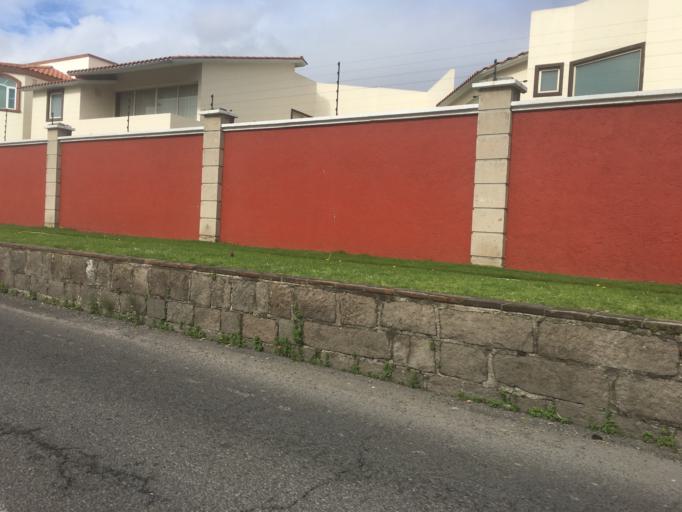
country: MX
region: Morelos
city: Metepec
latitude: 19.2674
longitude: -99.6073
